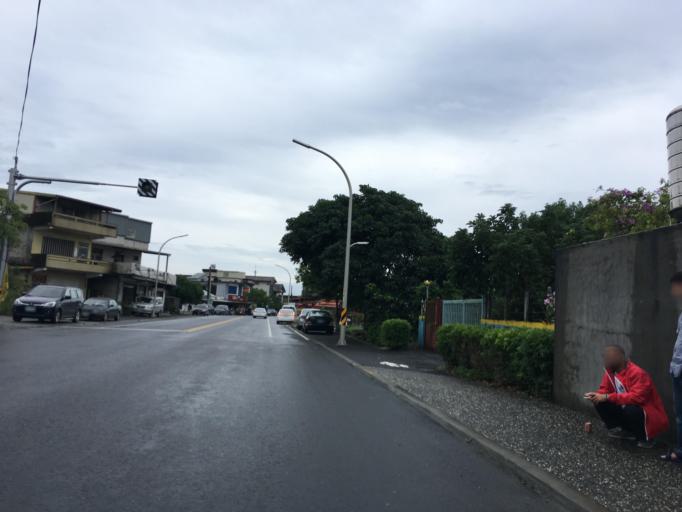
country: TW
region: Taiwan
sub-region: Yilan
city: Yilan
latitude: 24.6399
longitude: 121.8013
